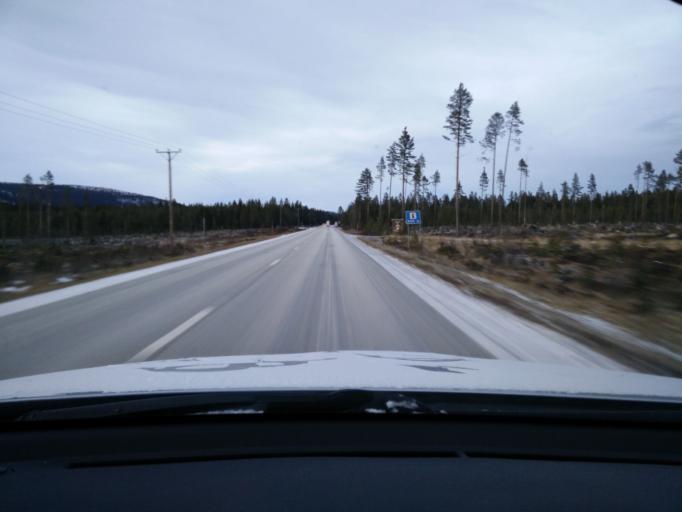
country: SE
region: Jaemtland
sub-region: Bergs Kommun
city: Hoverberg
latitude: 62.4987
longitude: 14.2081
